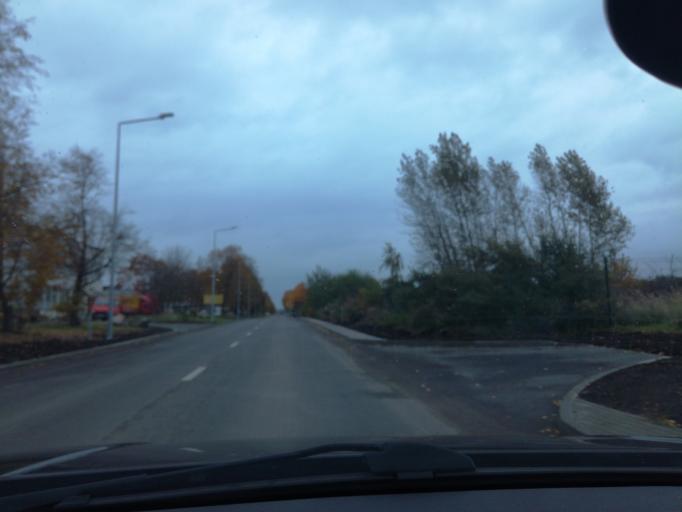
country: LT
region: Alytaus apskritis
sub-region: Alytus
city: Alytus
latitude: 54.4185
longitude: 24.0132
